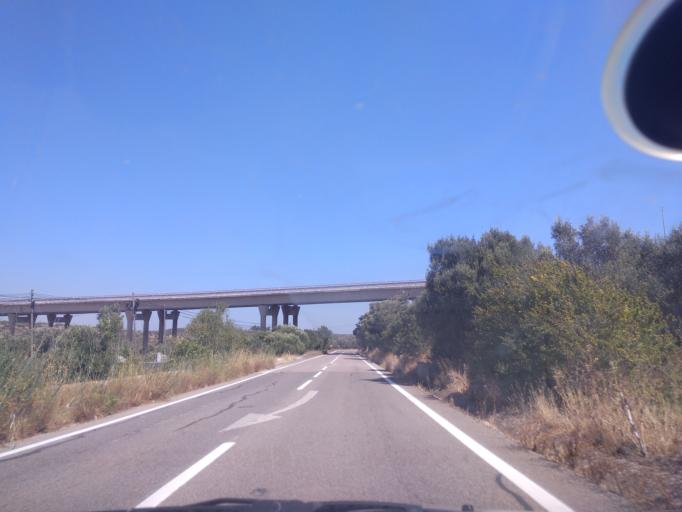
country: PT
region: Faro
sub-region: Lagos
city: Lagos
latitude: 37.1444
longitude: -8.7115
